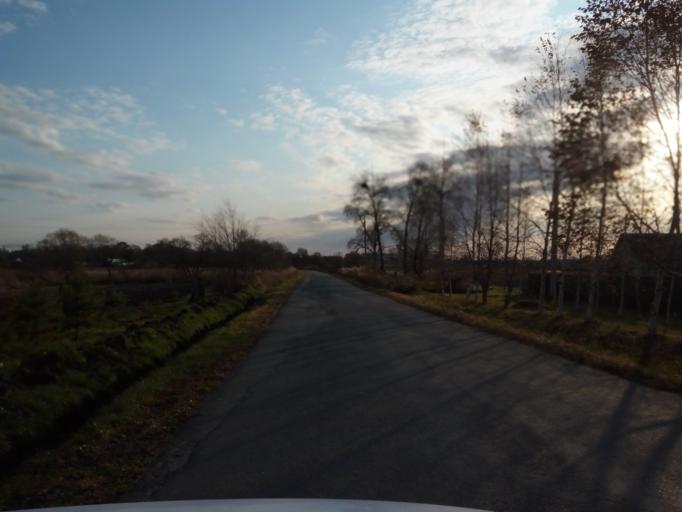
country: RU
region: Primorskiy
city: Lazo
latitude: 45.8274
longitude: 133.6144
